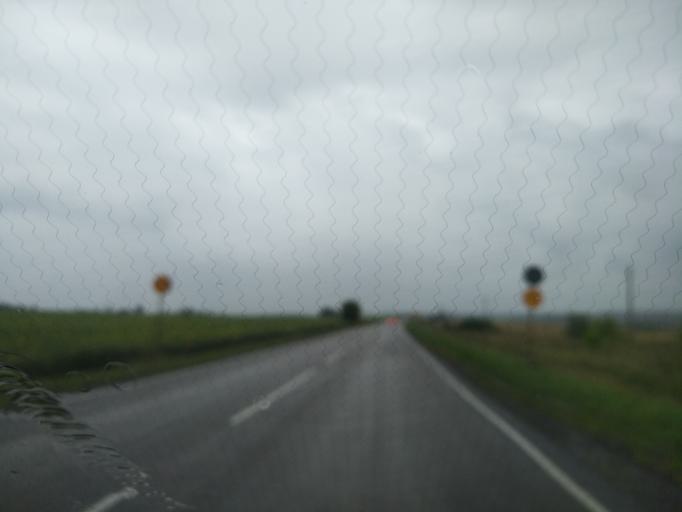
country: RU
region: Voronezj
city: Orlovo
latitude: 51.6785
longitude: 39.7933
